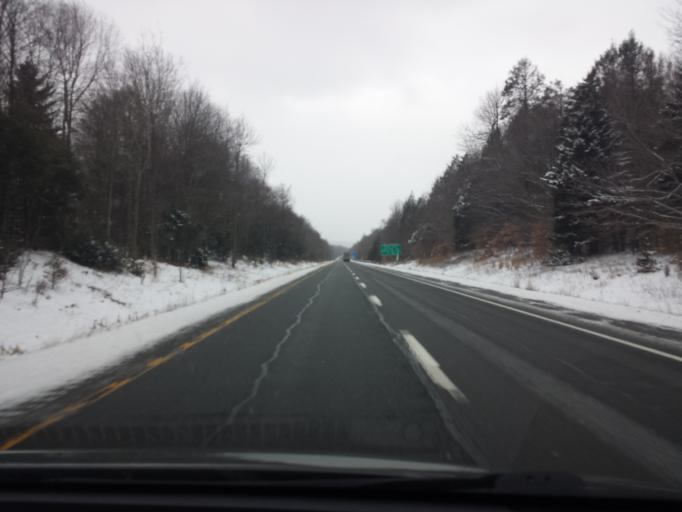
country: US
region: Pennsylvania
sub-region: Carbon County
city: Indian Mountain Lake
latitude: 41.0771
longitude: -75.5420
